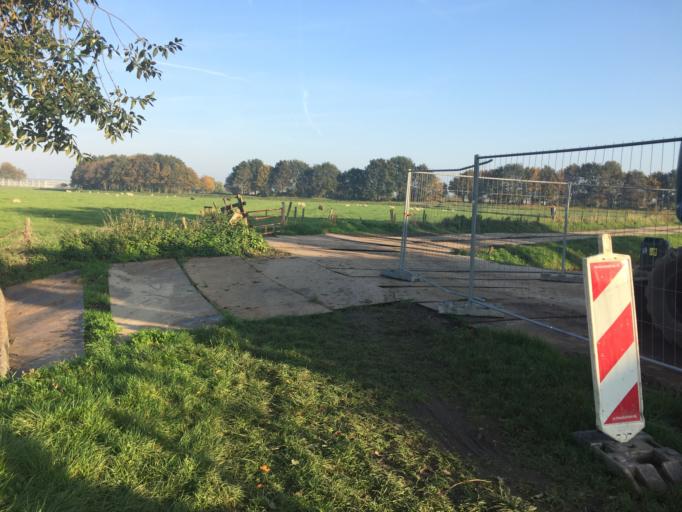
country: NL
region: South Holland
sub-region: Gemeente Lansingerland
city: Bergschenhoek
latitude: 52.0058
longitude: 4.4974
